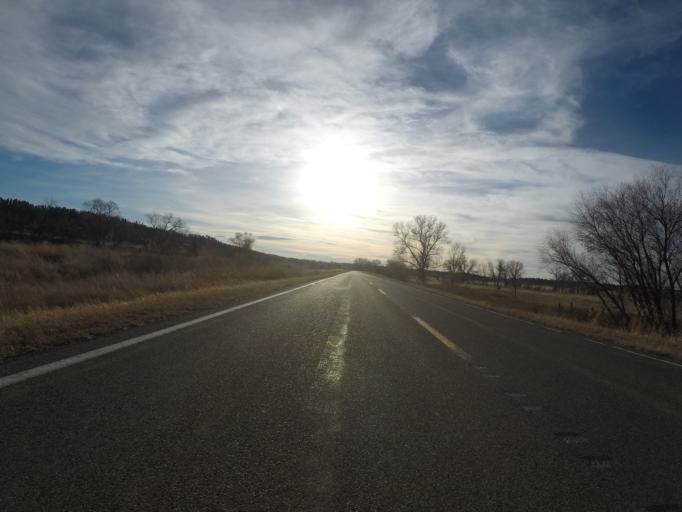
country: US
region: Montana
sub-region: Musselshell County
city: Roundup
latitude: 46.3463
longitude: -108.6805
